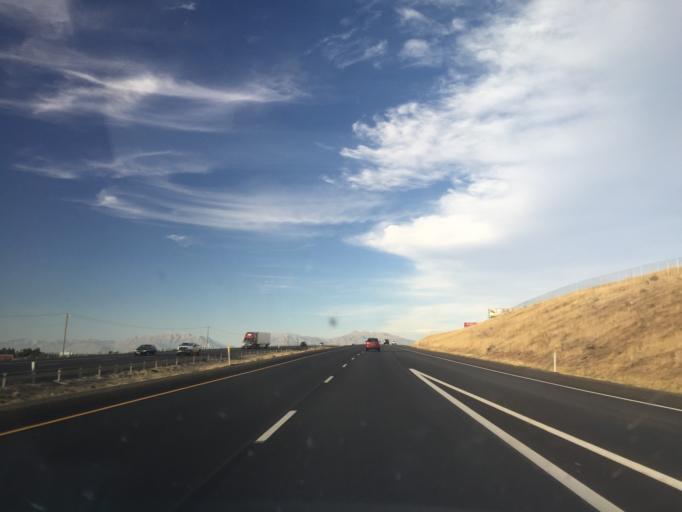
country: US
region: Utah
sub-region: Utah County
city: Santaquin
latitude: 39.9541
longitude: -111.7995
